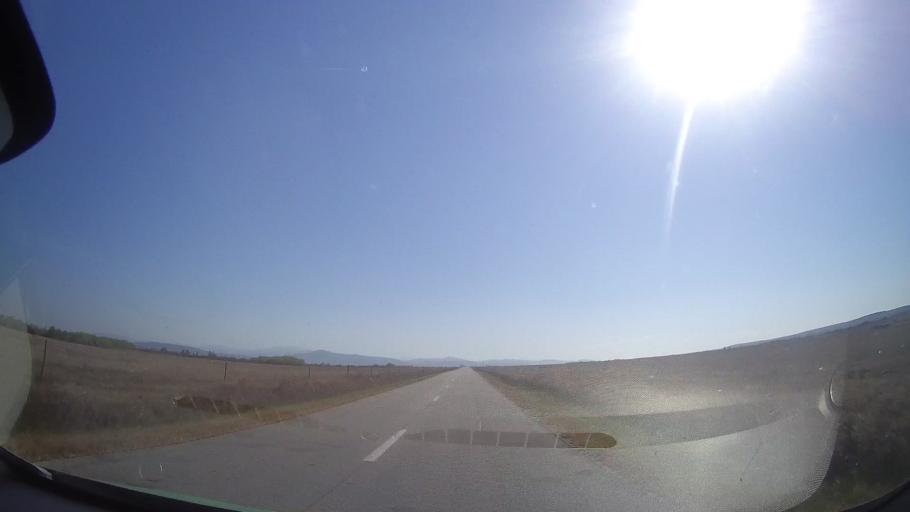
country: RO
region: Timis
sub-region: Comuna Traian Vuia
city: Traian Vuia
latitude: 45.7980
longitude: 22.0114
